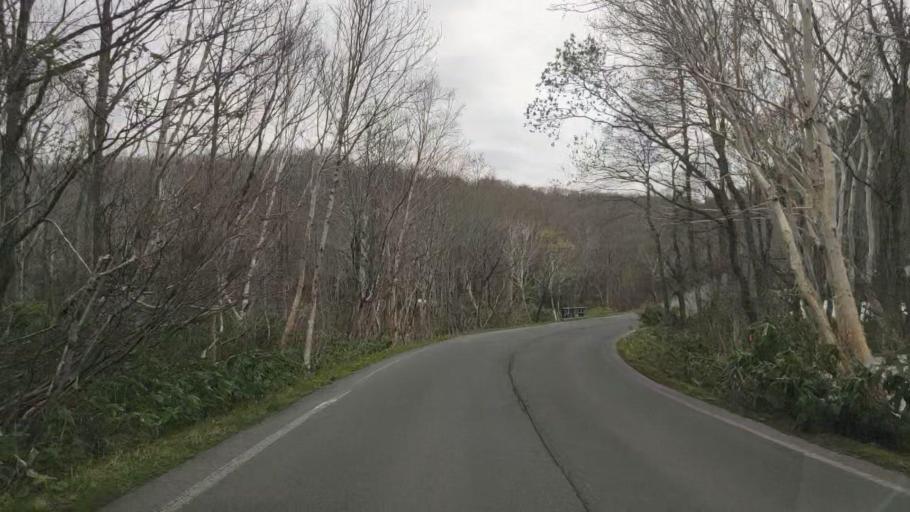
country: JP
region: Aomori
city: Aomori Shi
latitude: 40.6925
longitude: 140.9104
